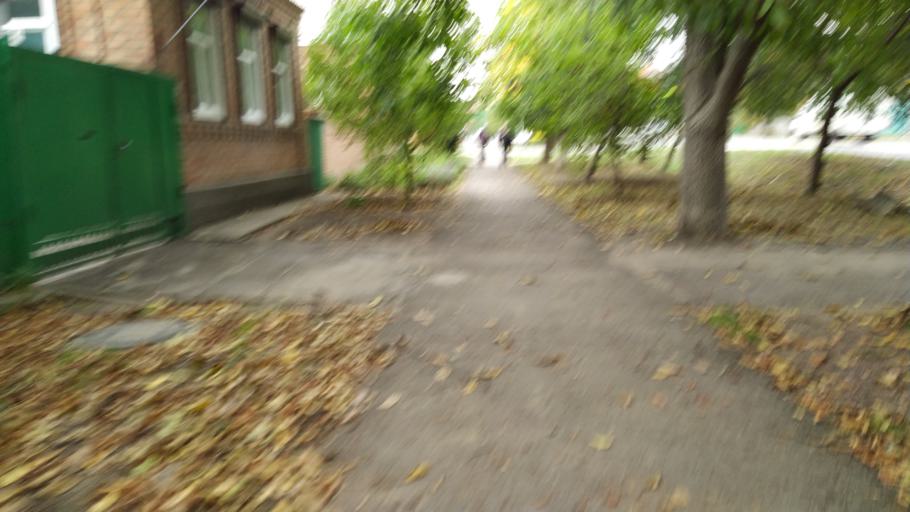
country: RU
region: Rostov
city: Bataysk
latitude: 47.1419
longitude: 39.7453
